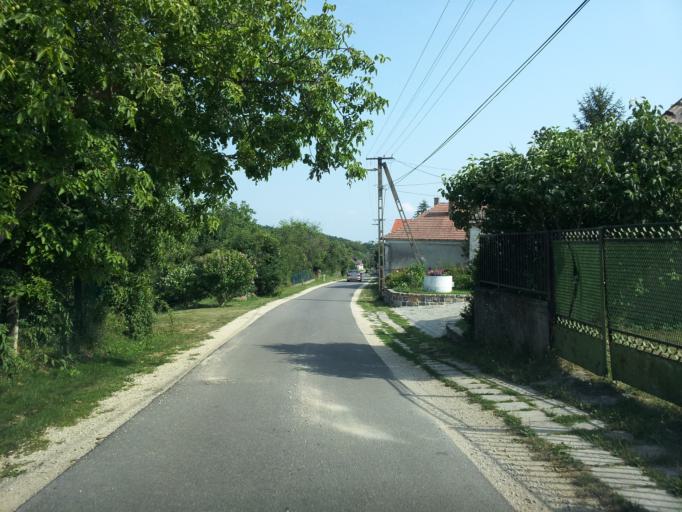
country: HU
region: Veszprem
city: Balatonfured
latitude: 47.0010
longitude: 17.8275
